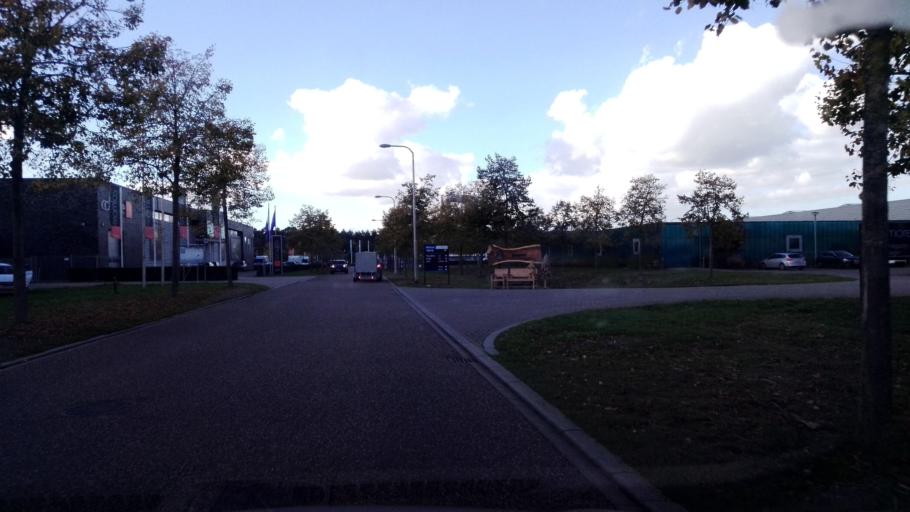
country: NL
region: Limburg
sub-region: Gemeente Venlo
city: Venlo
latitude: 51.3985
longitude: 6.1313
